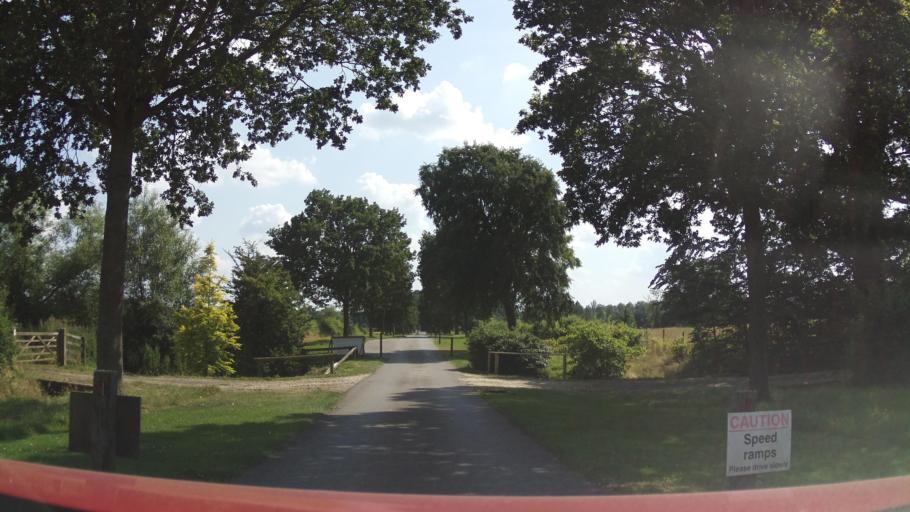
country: GB
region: England
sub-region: Gloucestershire
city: Moreton in Marsh
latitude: 51.9935
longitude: -1.7353
